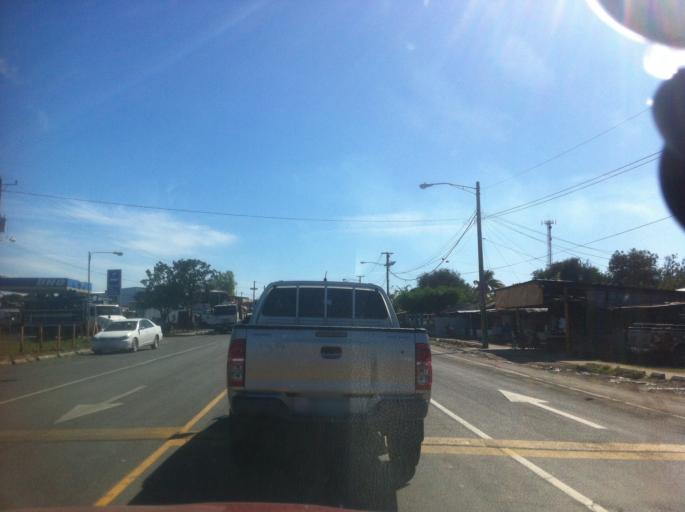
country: NI
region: Managua
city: Tipitapa
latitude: 12.3093
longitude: -86.0547
